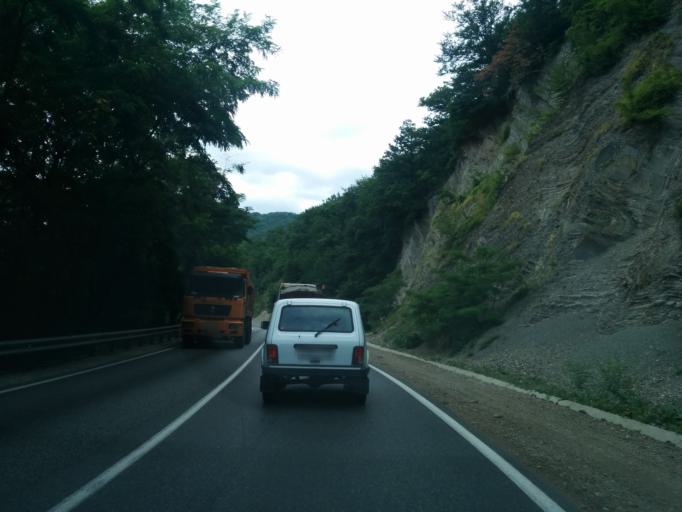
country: RU
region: Krasnodarskiy
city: Agoy
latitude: 44.1339
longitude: 39.0501
